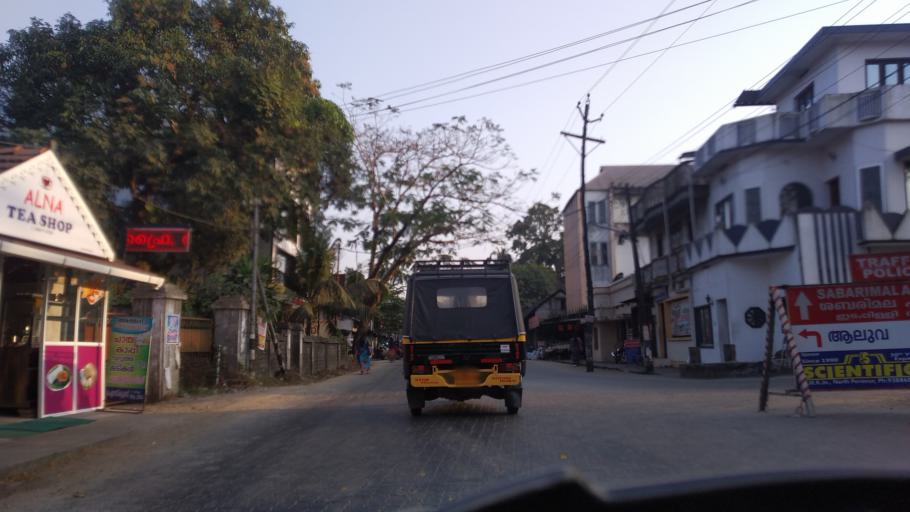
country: IN
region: Kerala
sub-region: Thrissur District
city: Kodungallur
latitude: 10.1509
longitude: 76.2234
